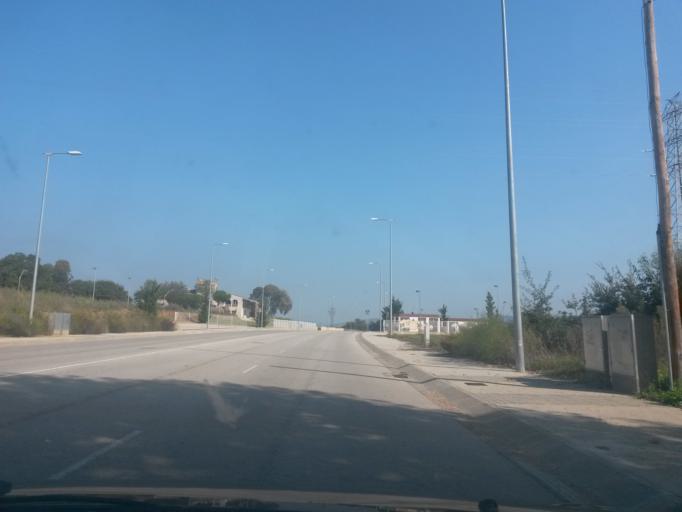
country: ES
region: Catalonia
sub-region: Provincia de Girona
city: Fornells de la Selva
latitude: 41.9398
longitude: 2.7975
